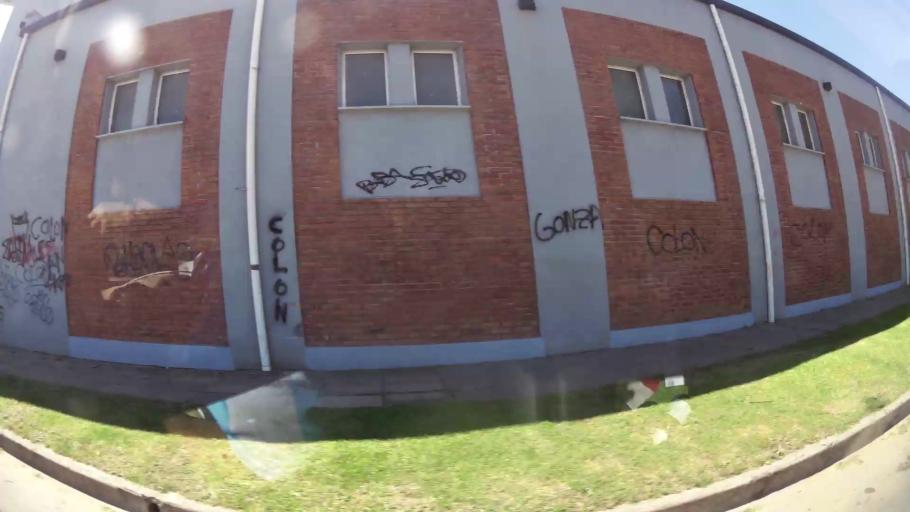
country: AR
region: Santa Fe
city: Santa Fe de la Vera Cruz
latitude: -31.6444
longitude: -60.6895
